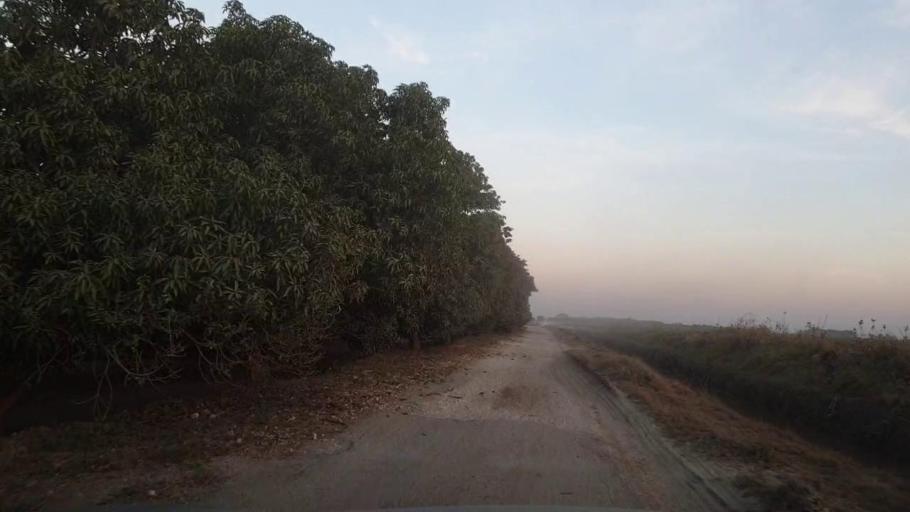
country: PK
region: Sindh
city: Tando Allahyar
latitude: 25.5647
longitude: 68.7617
